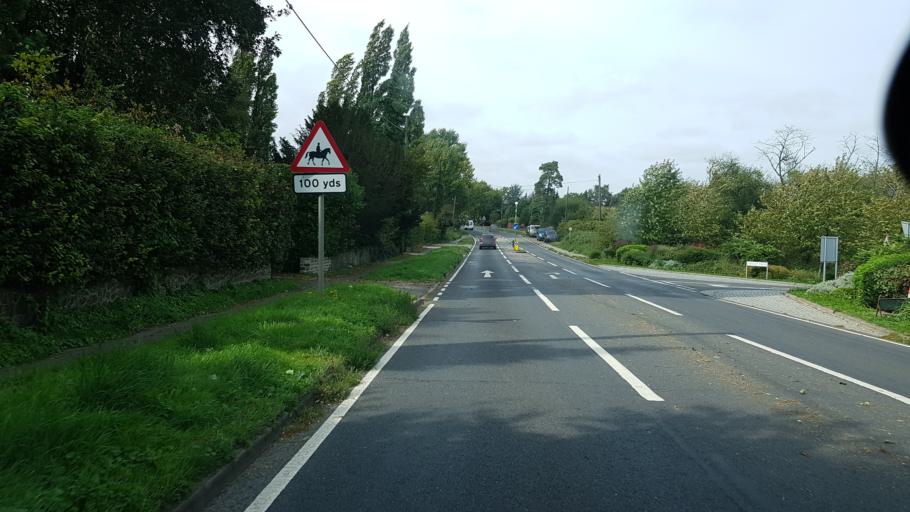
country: GB
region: England
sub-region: Kent
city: West Malling
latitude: 51.3016
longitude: 0.3995
